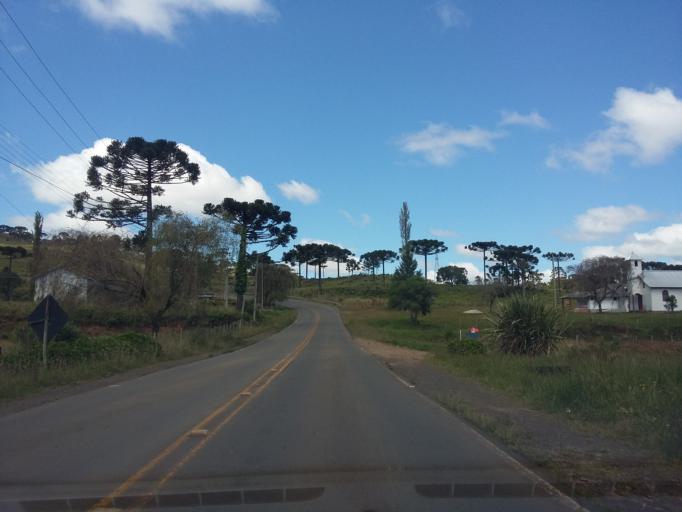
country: BR
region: Santa Catarina
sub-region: Sao Joaquim
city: Sao Joaquim
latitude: -28.2687
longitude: -49.7607
